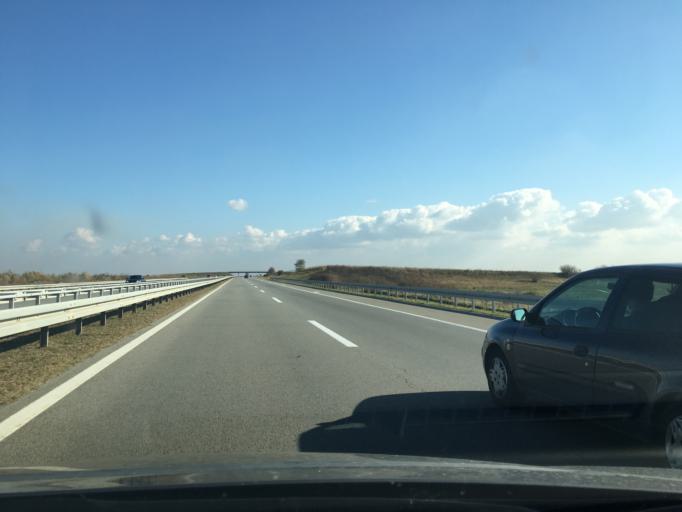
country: RS
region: Autonomna Pokrajina Vojvodina
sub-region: Juznobacki Okrug
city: Kovilj
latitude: 45.2612
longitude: 19.9874
